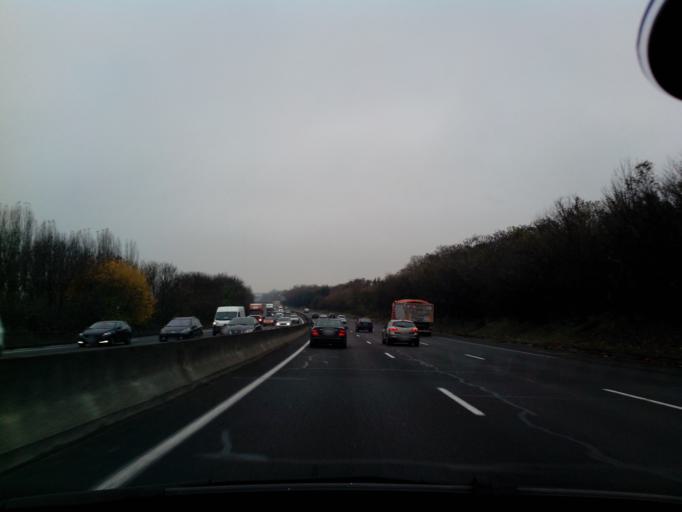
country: FR
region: Ile-de-France
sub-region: Departement de l'Essonne
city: Longjumeau
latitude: 48.6936
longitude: 2.3202
